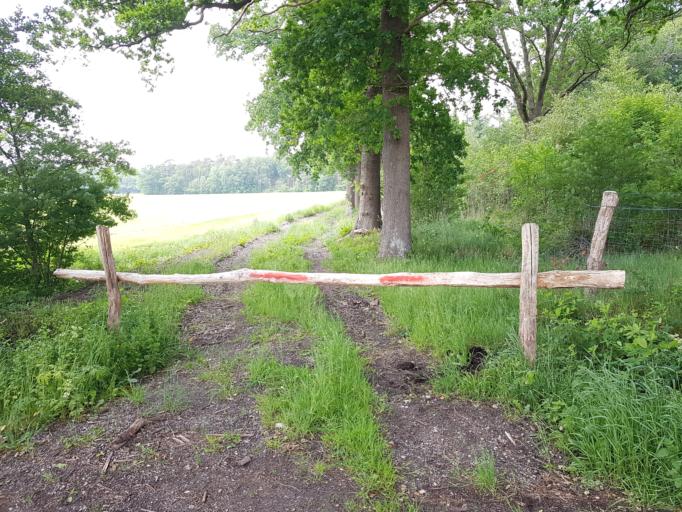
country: NL
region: Friesland
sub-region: Gemeente Heerenveen
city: Jubbega
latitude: 53.0285
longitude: 6.0981
